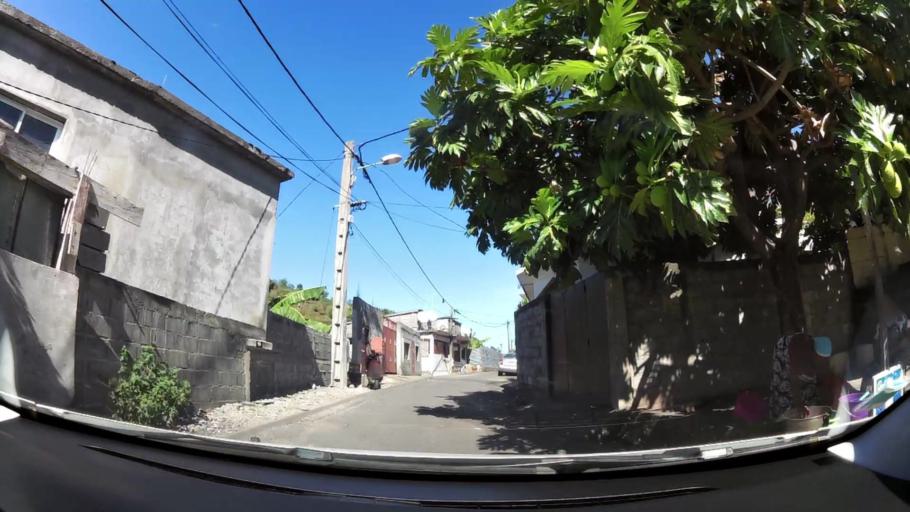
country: YT
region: Pamandzi
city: Pamandzi
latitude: -12.7899
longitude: 45.2706
